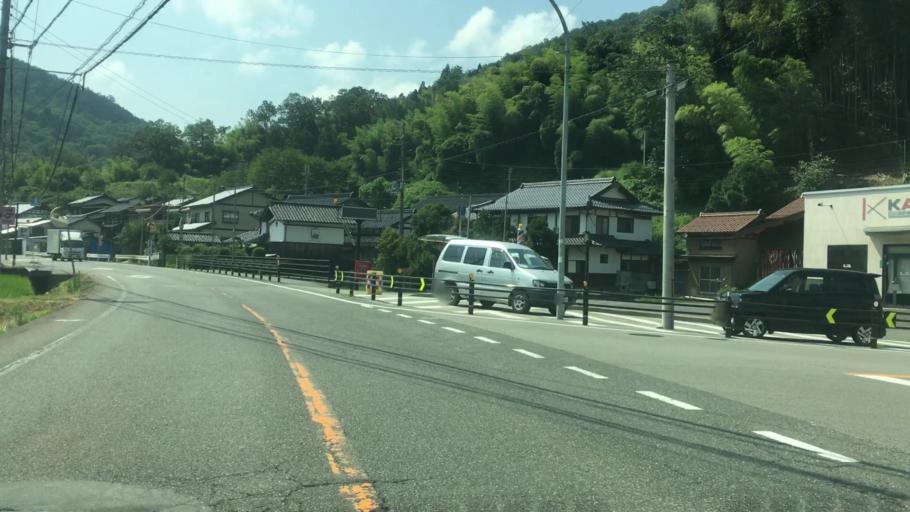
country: JP
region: Hyogo
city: Toyooka
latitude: 35.5669
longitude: 134.7876
